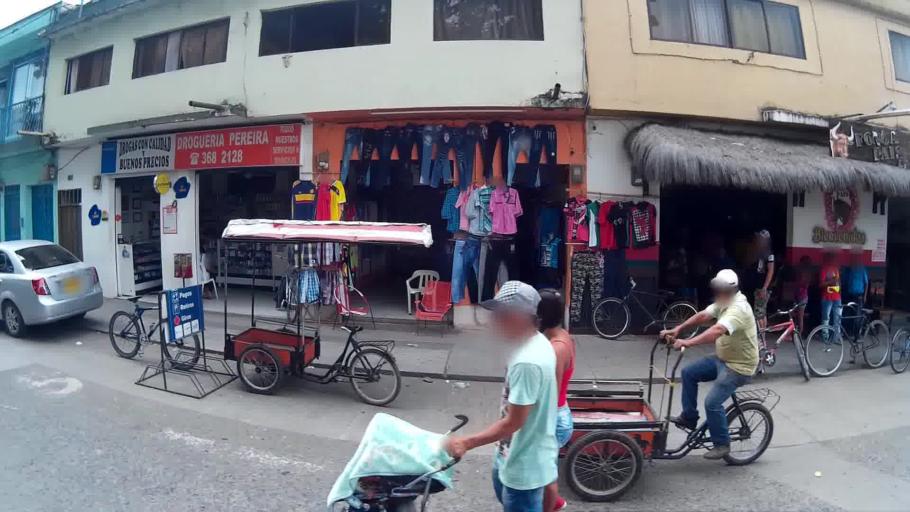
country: CO
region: Risaralda
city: La Virginia
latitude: 4.8961
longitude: -75.8843
